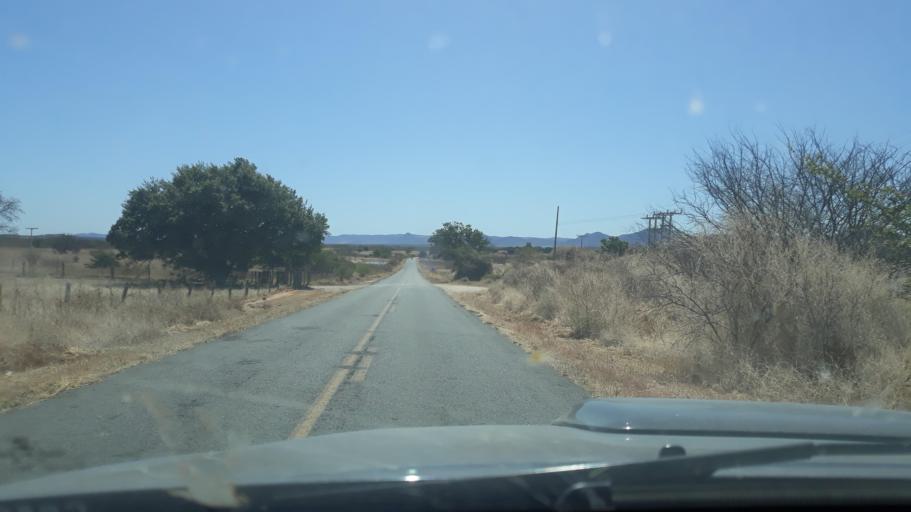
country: BR
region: Bahia
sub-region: Guanambi
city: Guanambi
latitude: -13.9689
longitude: -42.8549
